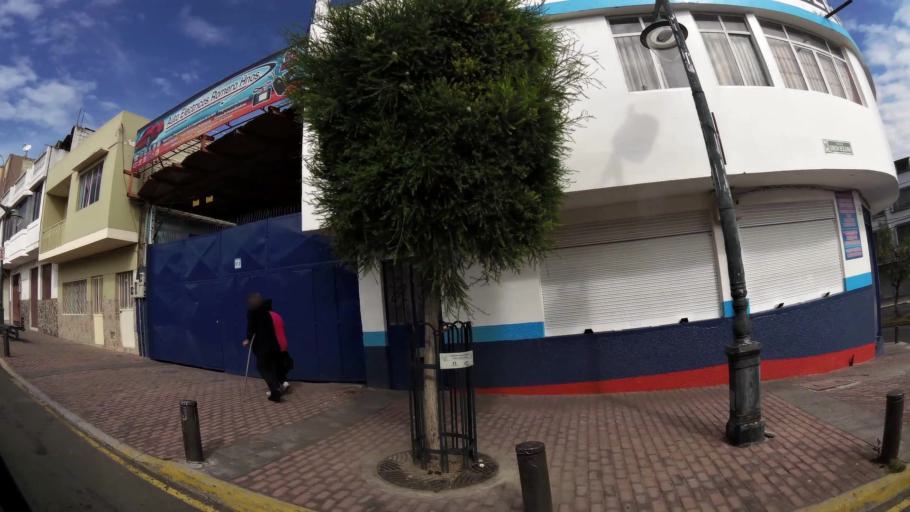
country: EC
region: Tungurahua
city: Ambato
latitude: -1.2370
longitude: -78.6244
